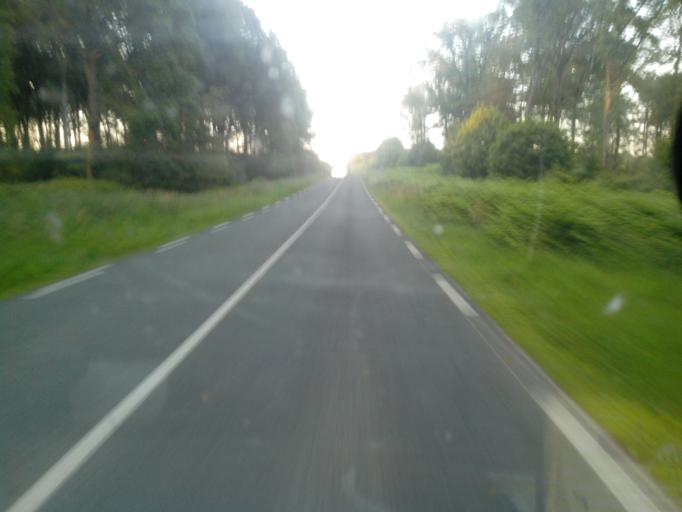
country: FR
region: Brittany
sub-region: Departement d'Ille-et-Vilaine
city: Fougeres
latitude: 48.3726
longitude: -1.1788
